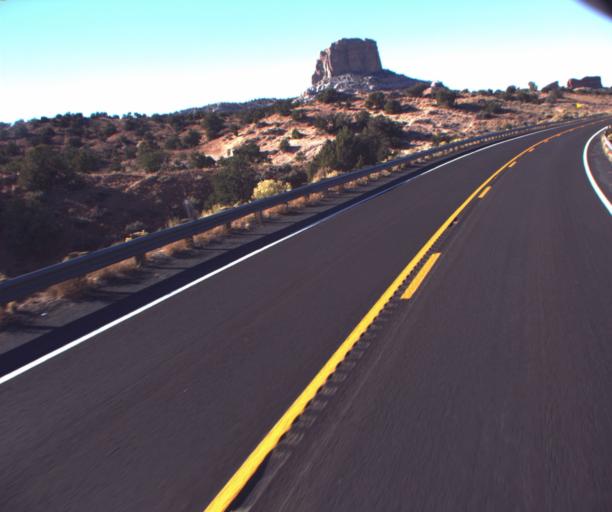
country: US
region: Arizona
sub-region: Coconino County
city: Kaibito
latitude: 36.5967
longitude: -110.9115
